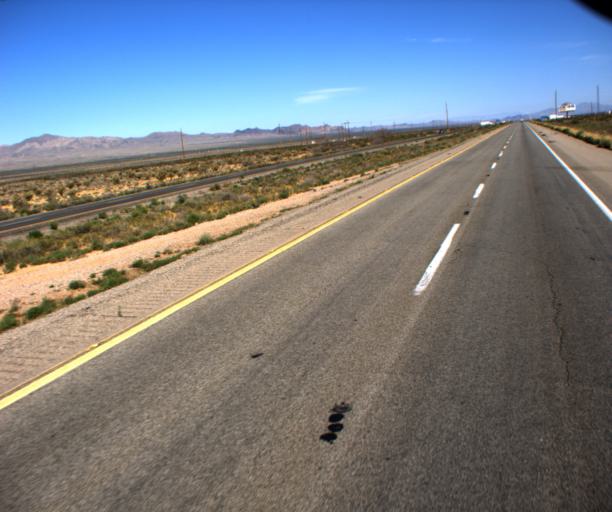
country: US
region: Arizona
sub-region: Mohave County
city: Dolan Springs
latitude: 35.5285
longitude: -114.3514
